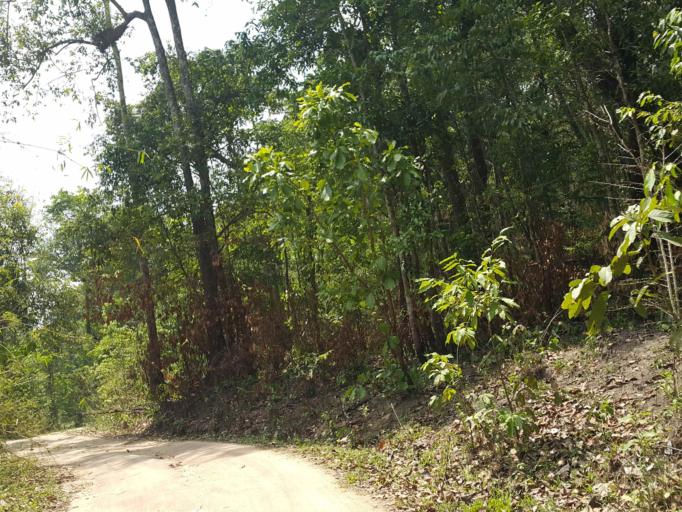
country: TH
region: Chiang Mai
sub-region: Amphoe Chiang Dao
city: Chiang Dao
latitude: 19.3011
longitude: 98.7497
